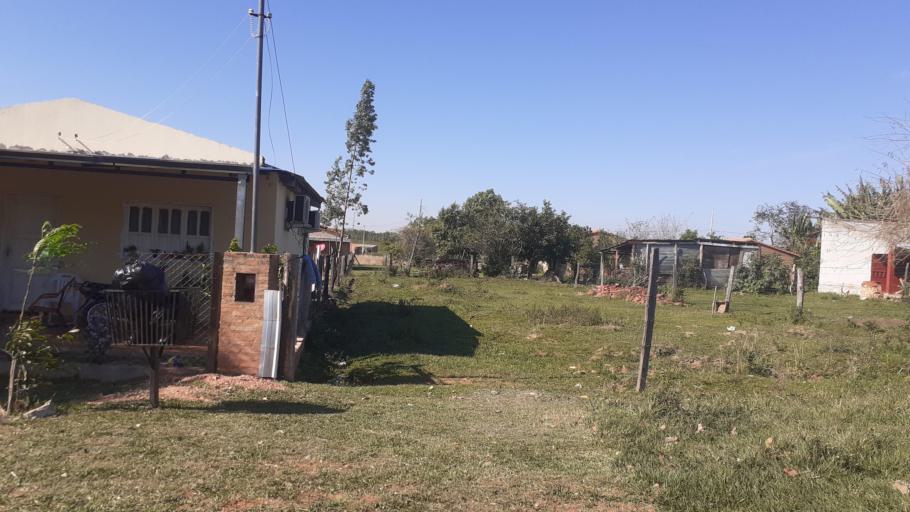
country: PY
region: Misiones
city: San Juan Bautista
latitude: -26.6648
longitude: -57.1236
